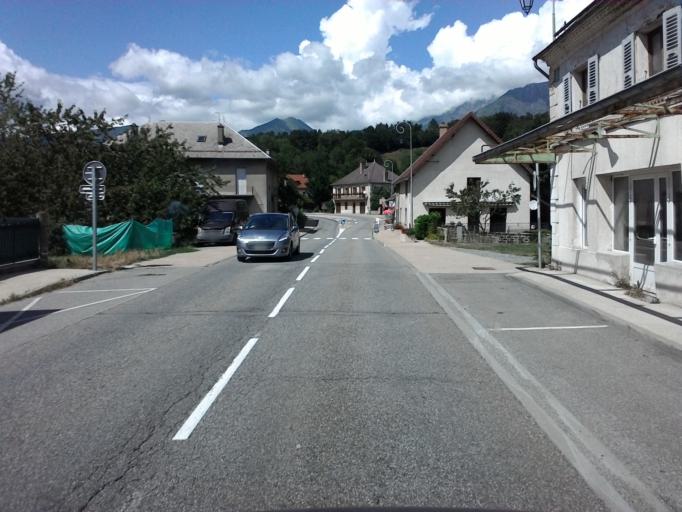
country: FR
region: Provence-Alpes-Cote d'Azur
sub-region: Departement des Hautes-Alpes
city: Saint-Bonnet-en-Champsaur
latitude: 44.7543
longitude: 6.0090
